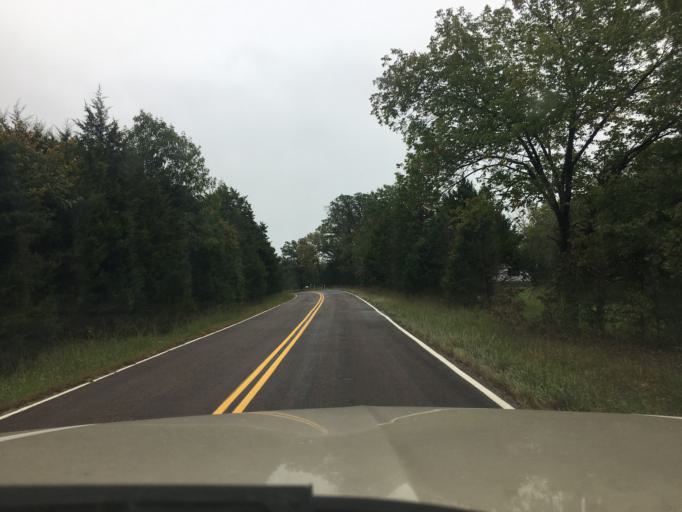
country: US
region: Missouri
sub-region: Crawford County
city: Cuba
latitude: 38.1909
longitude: -91.4725
